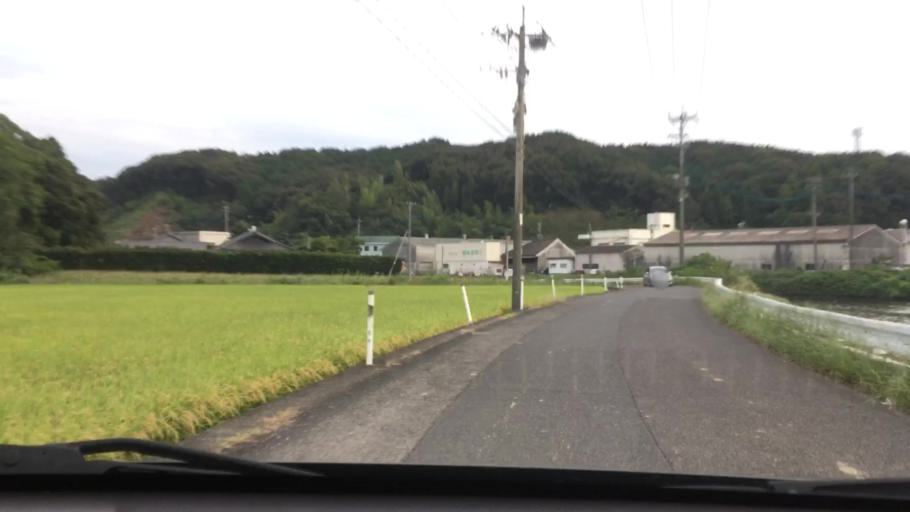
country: JP
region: Nagasaki
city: Togitsu
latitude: 32.9894
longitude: 129.7734
